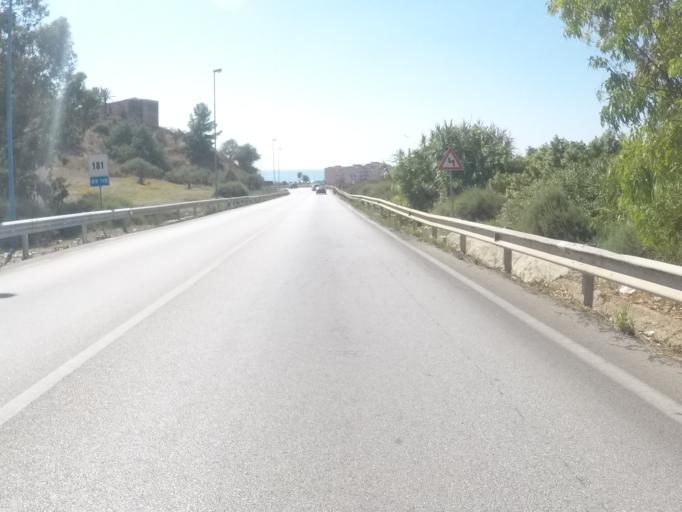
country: IT
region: Sicily
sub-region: Agrigento
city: Porto Empedocle
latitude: 37.2941
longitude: 13.5216
